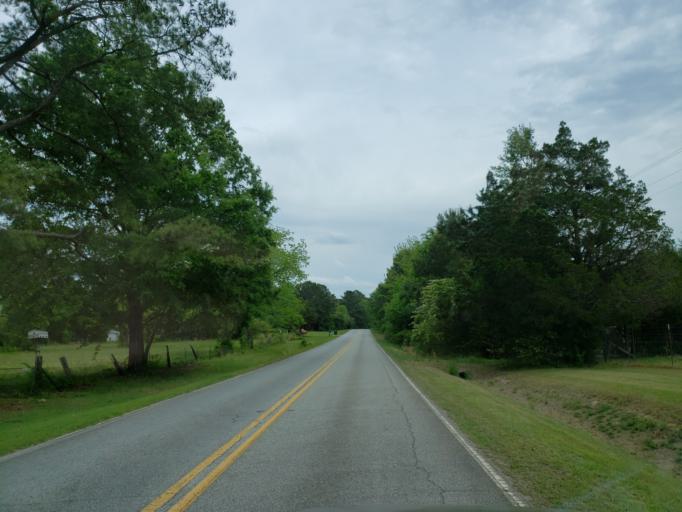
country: US
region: Georgia
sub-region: Bibb County
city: West Point
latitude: 32.8310
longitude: -83.8889
